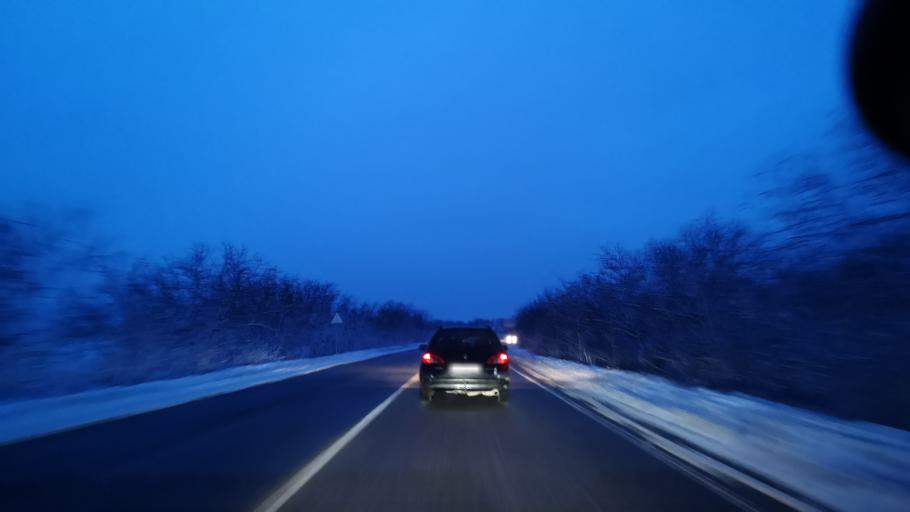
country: MD
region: Orhei
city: Orhei
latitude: 47.5594
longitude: 28.7994
